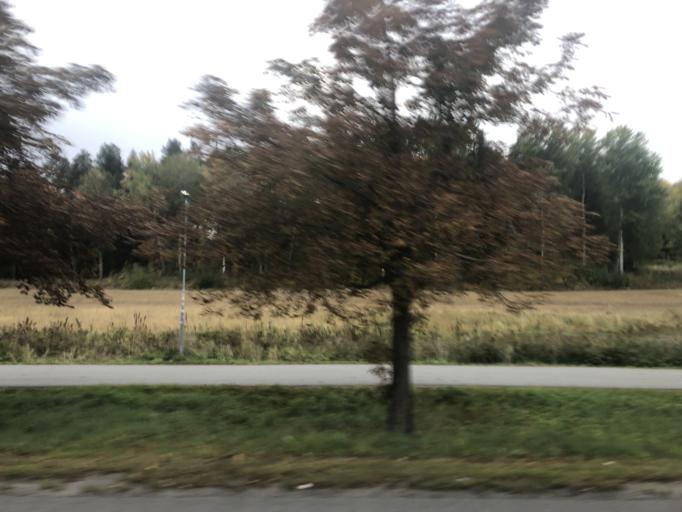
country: SE
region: Stockholm
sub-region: Jarfalla Kommun
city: Jakobsberg
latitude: 59.4169
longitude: 17.8222
